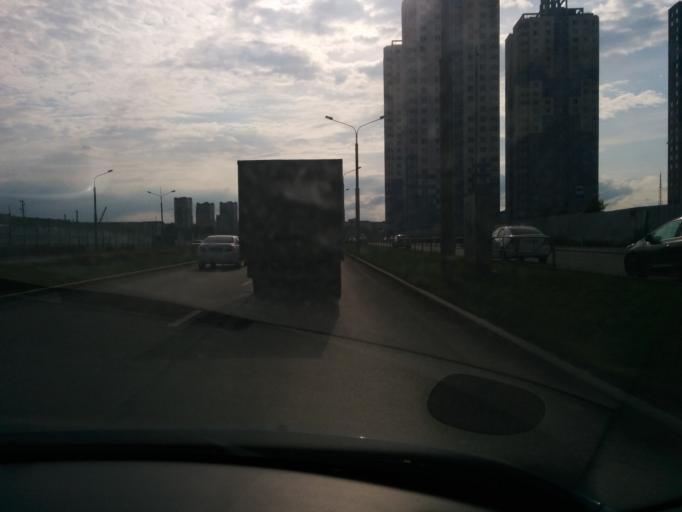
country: RU
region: Perm
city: Perm
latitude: 58.0050
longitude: 56.3252
